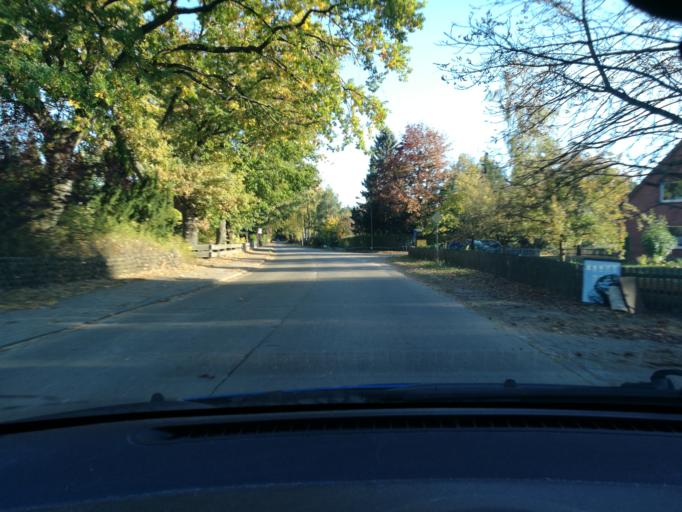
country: DE
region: Lower Saxony
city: Bleckede
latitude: 53.2819
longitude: 10.7549
